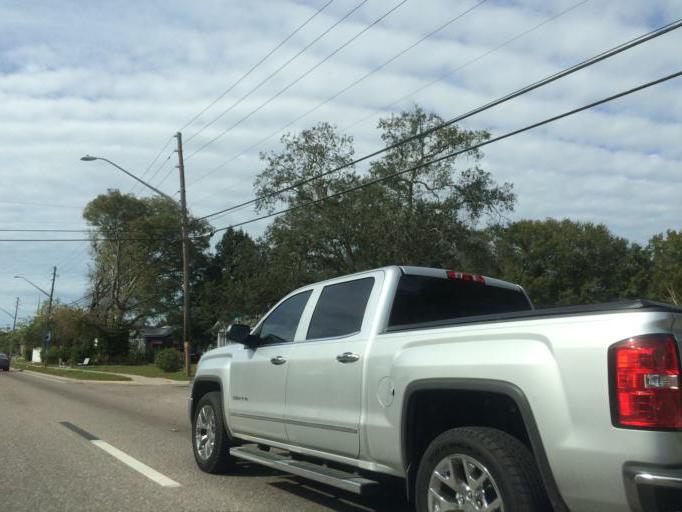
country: US
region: Florida
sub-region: Pinellas County
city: West and East Lealman
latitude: 27.8065
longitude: -82.6894
